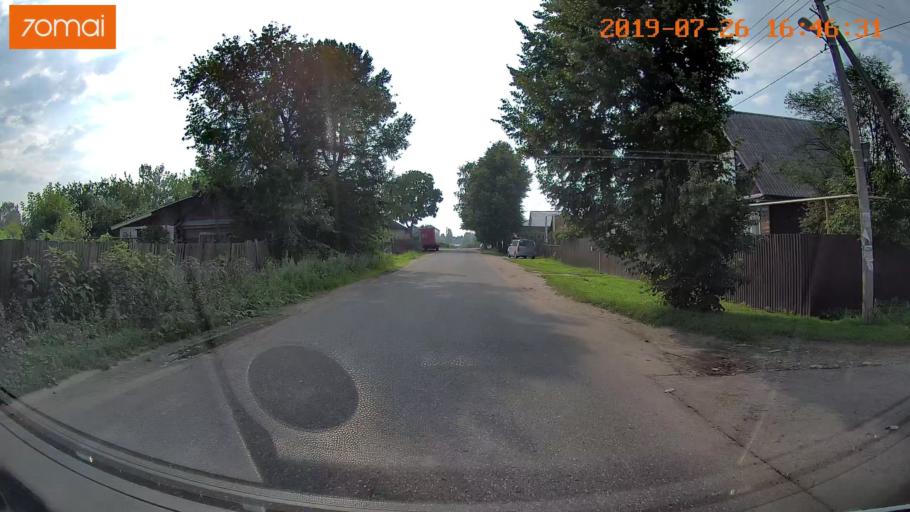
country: RU
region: Ivanovo
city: Bogorodskoye
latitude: 57.0450
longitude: 41.0162
